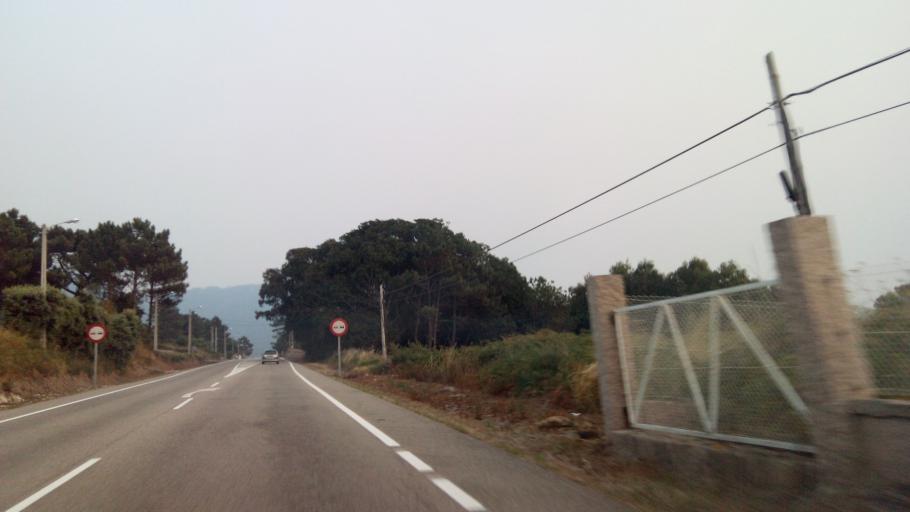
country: ES
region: Galicia
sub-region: Provincia de Pontevedra
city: Oia
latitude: 42.0229
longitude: -8.8830
